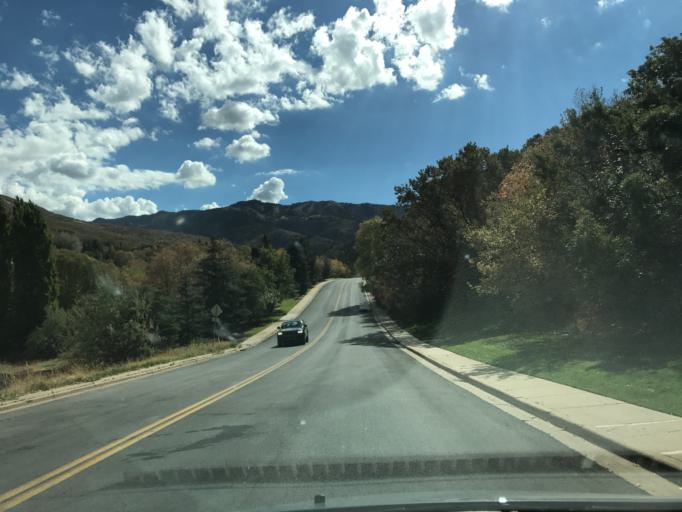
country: US
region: Utah
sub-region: Davis County
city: Bountiful
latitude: 40.8685
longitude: -111.8466
